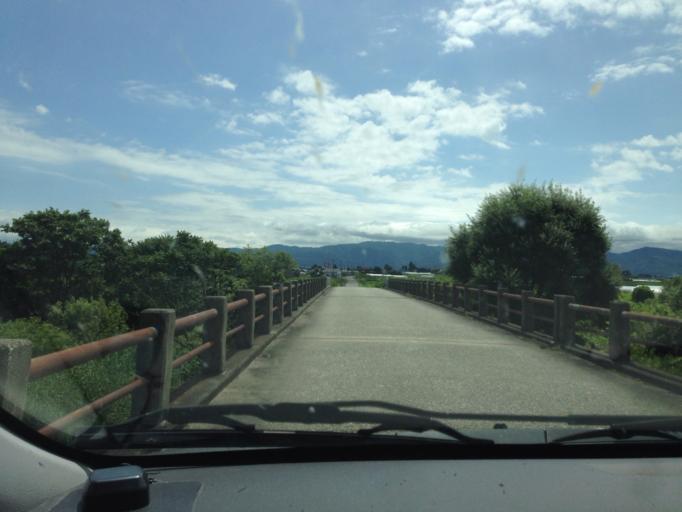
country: JP
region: Fukushima
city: Kitakata
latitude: 37.5153
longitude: 139.8458
